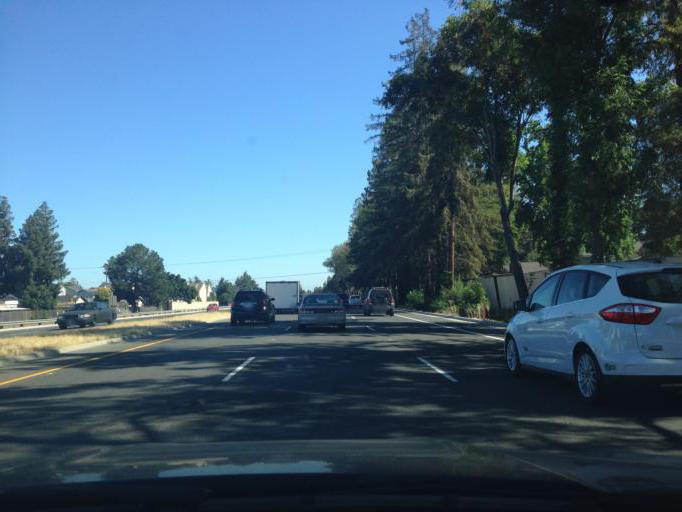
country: US
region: California
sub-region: Santa Clara County
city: Campbell
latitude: 37.2894
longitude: -121.9604
